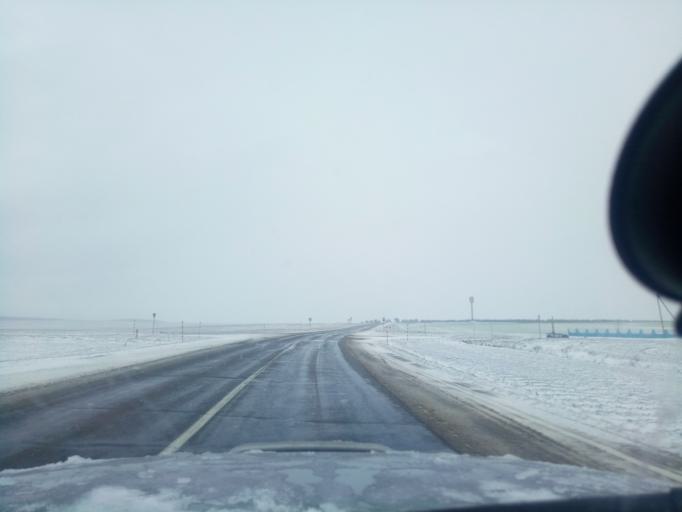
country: BY
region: Minsk
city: Haradzyeya
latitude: 53.3011
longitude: 26.5754
